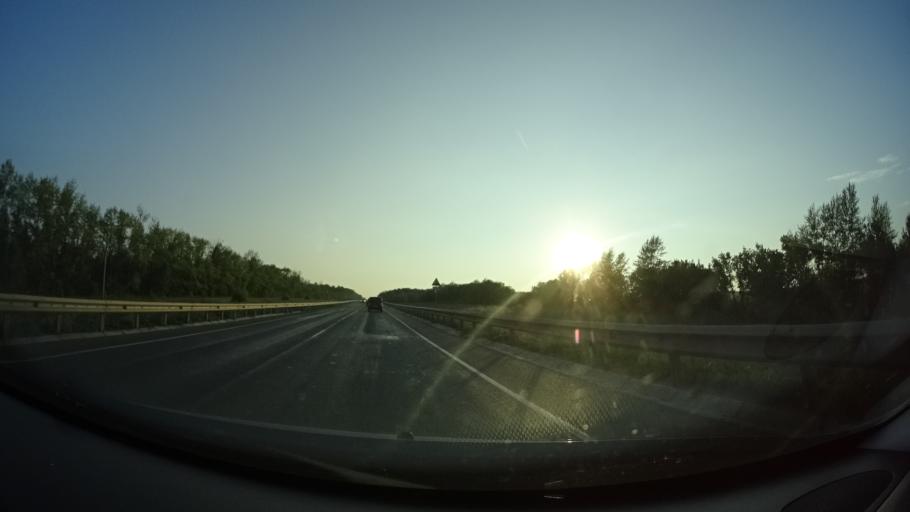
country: RU
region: Samara
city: Isakly
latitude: 54.0129
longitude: 51.7096
